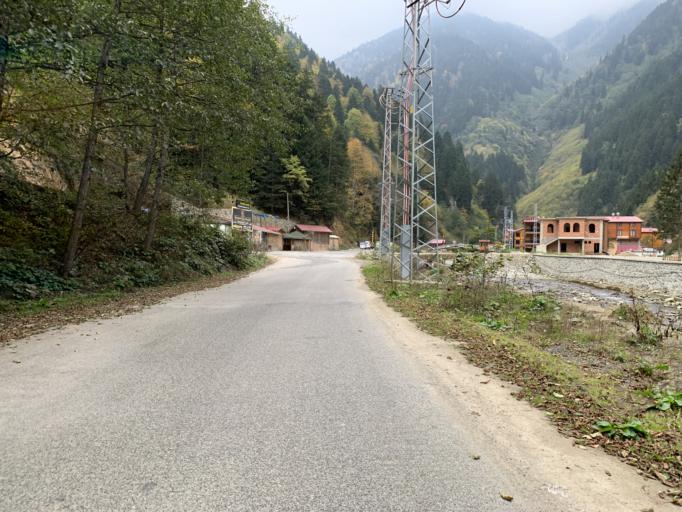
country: TR
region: Trabzon
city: Uzungol
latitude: 40.5985
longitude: 40.3212
